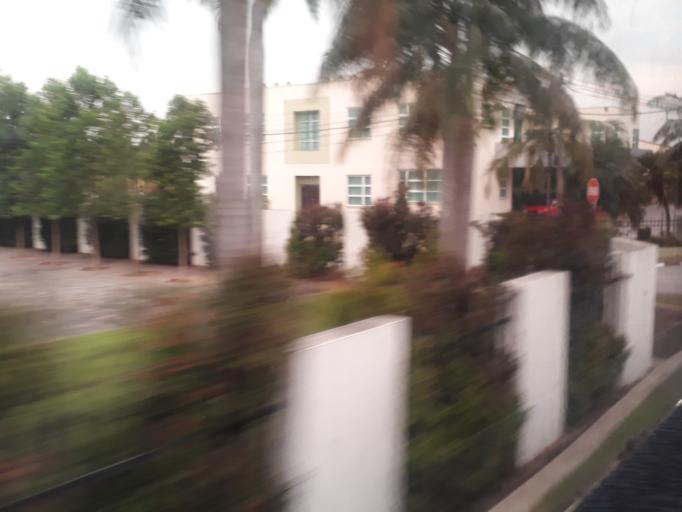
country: MY
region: Perak
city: Ipoh
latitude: 4.6021
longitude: 101.1178
